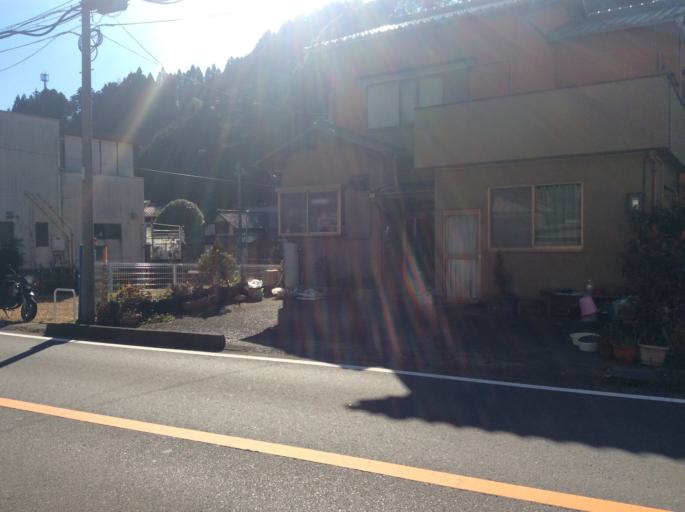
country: JP
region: Shizuoka
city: Fujinomiya
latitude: 35.1192
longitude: 138.5108
